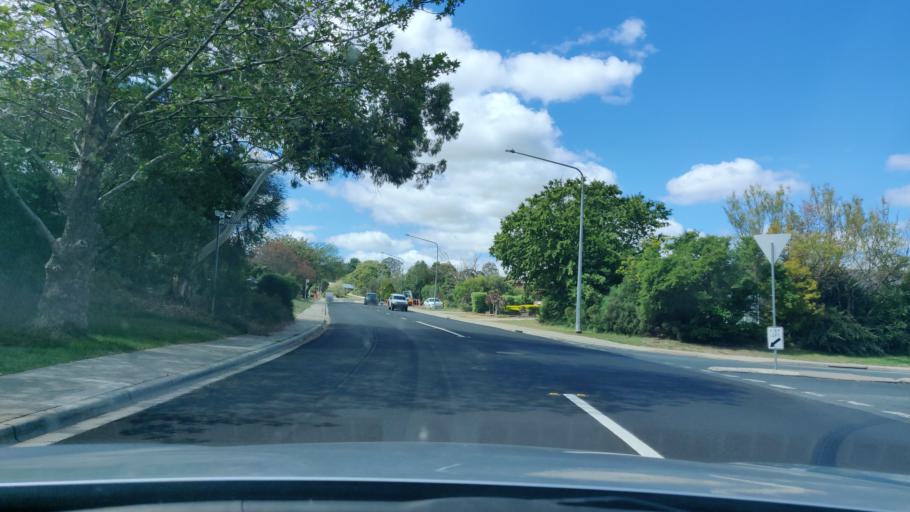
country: AU
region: Australian Capital Territory
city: Macarthur
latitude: -35.4358
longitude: 149.0975
